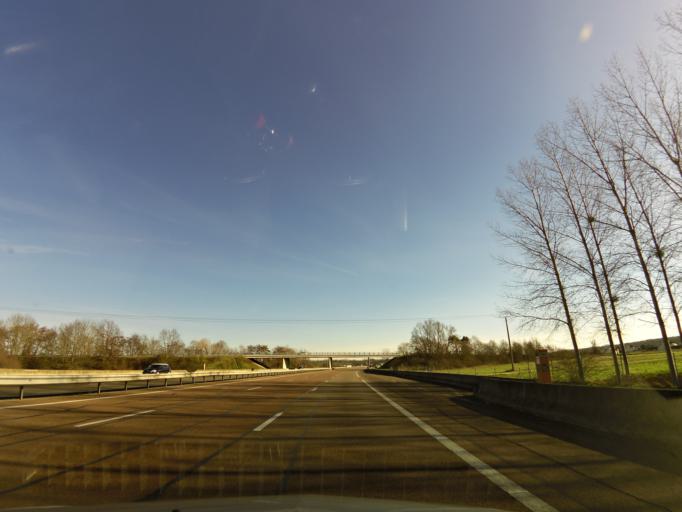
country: FR
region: Bourgogne
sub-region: Departement de l'Yonne
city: Appoigny
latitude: 47.8637
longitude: 3.5266
